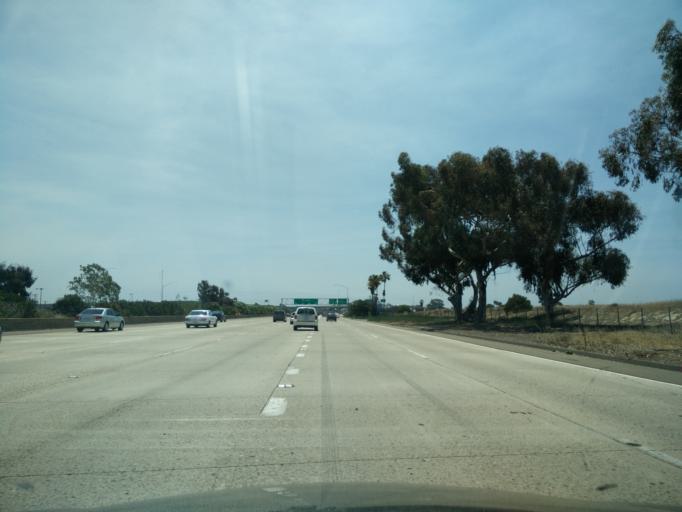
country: US
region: California
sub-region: San Diego County
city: San Diego
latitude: 32.7662
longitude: -117.2059
